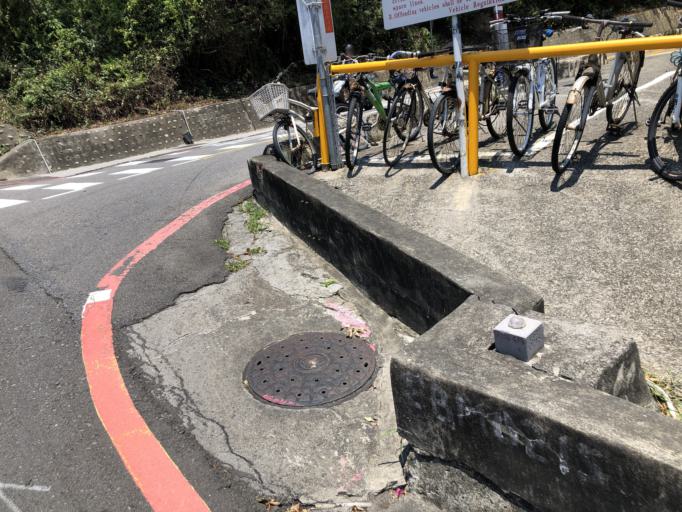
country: TW
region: Kaohsiung
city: Kaohsiung
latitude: 22.6287
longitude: 120.2635
